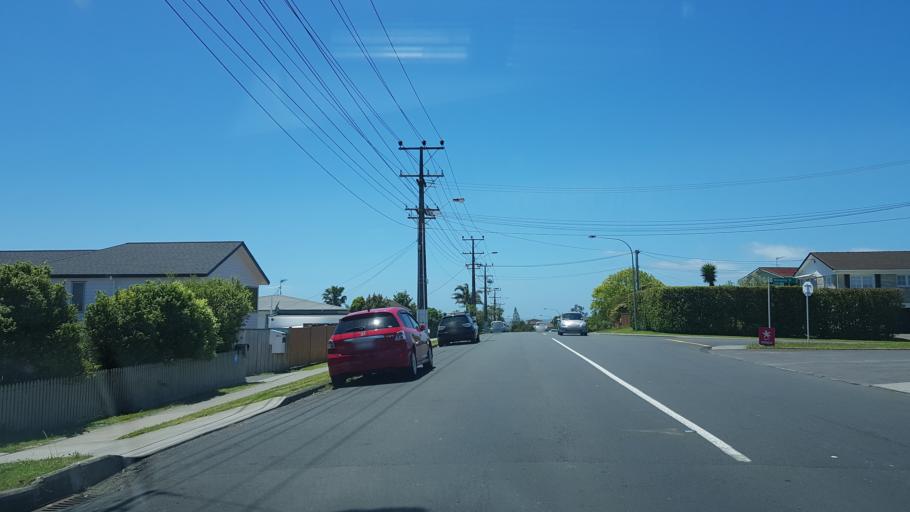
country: NZ
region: Auckland
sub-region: Auckland
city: North Shore
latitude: -36.7896
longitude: 174.7346
